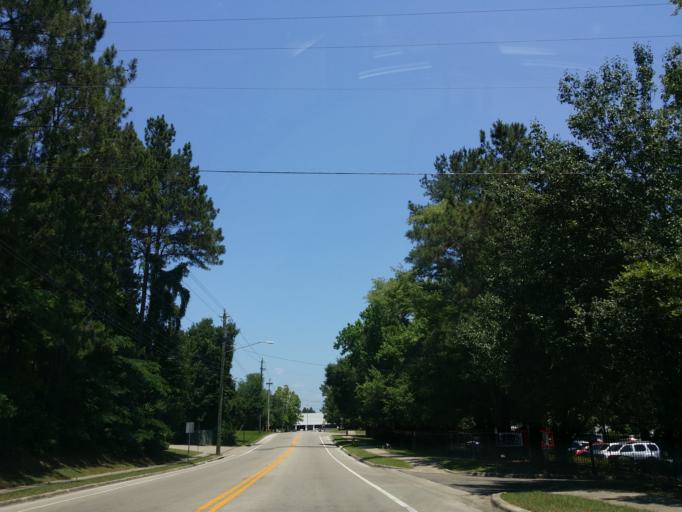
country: US
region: Florida
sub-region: Leon County
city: Tallahassee
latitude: 30.4710
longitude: -84.3493
